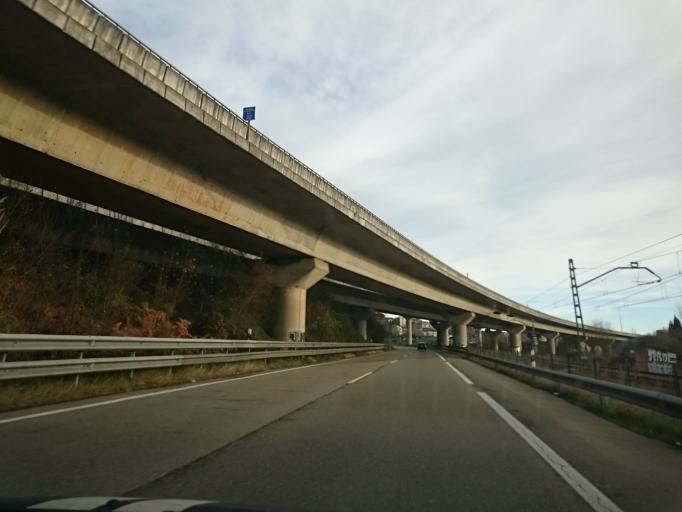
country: ES
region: Asturias
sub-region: Province of Asturias
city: Oviedo
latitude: 43.3460
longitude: -5.8612
